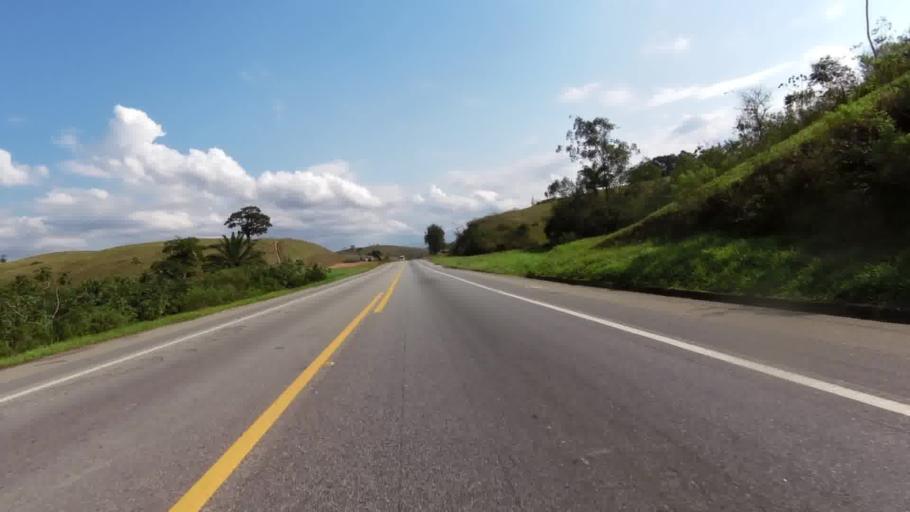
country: BR
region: Rio de Janeiro
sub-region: Macae
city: Macae
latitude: -22.2549
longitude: -41.8315
